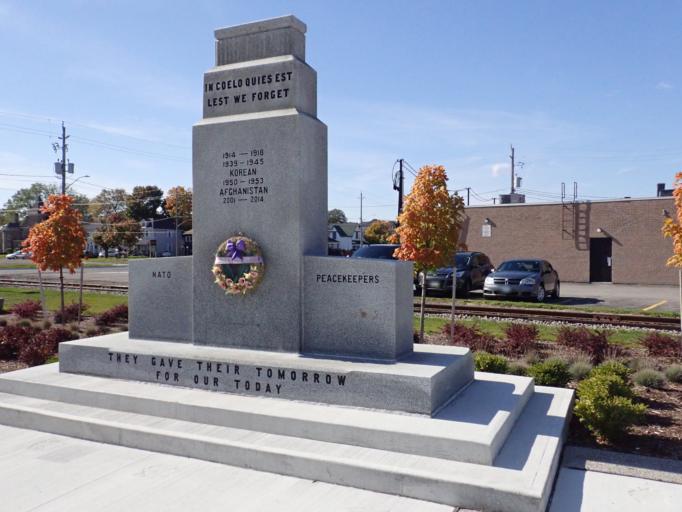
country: CA
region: Ontario
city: St. Thomas
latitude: 42.7781
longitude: -81.1909
